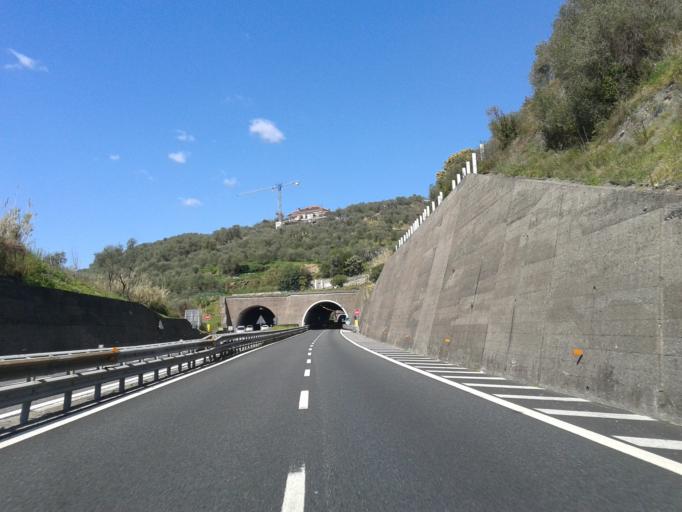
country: IT
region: Liguria
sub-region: Provincia di Genova
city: San Salvatore
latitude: 44.3212
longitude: 9.3405
